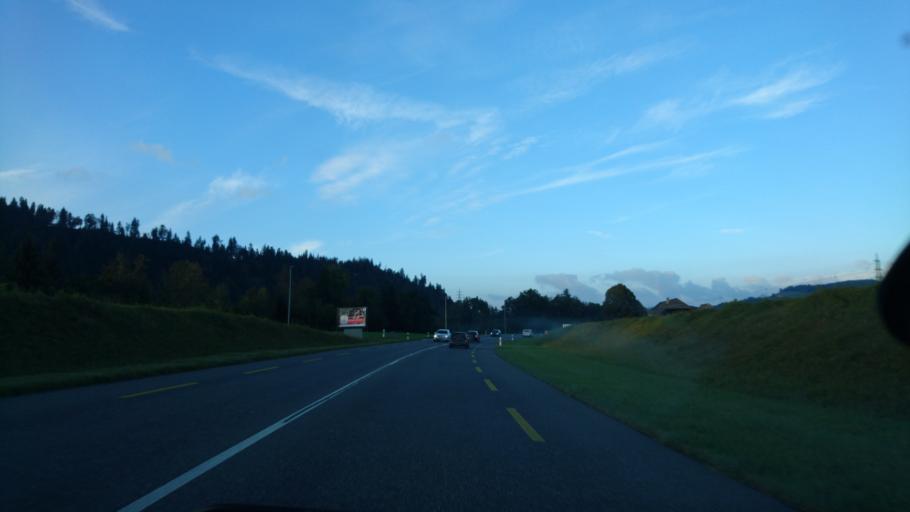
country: CH
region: Bern
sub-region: Emmental District
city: Signau
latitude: 46.9323
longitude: 7.7403
